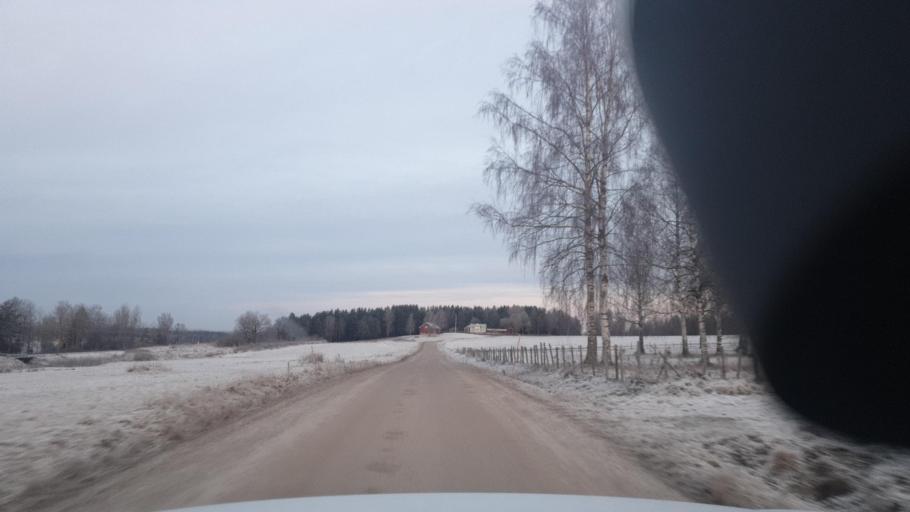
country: SE
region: Vaermland
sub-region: Eda Kommun
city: Amotfors
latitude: 59.8050
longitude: 12.3632
